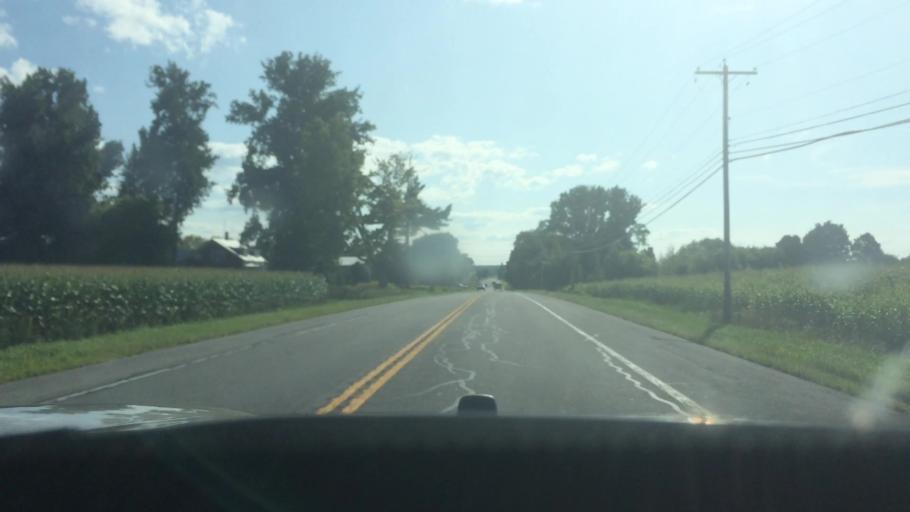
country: US
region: New York
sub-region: Franklin County
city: Malone
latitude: 44.8359
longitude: -74.3207
